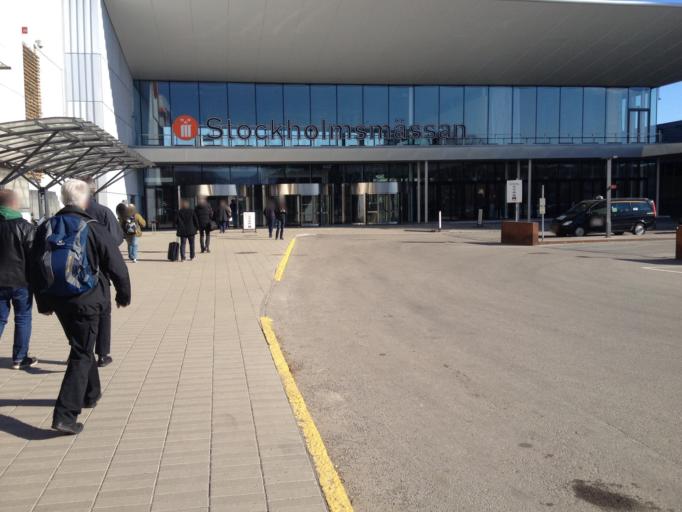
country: SE
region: Stockholm
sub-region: Stockholms Kommun
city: Arsta
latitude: 59.2773
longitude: 18.0145
